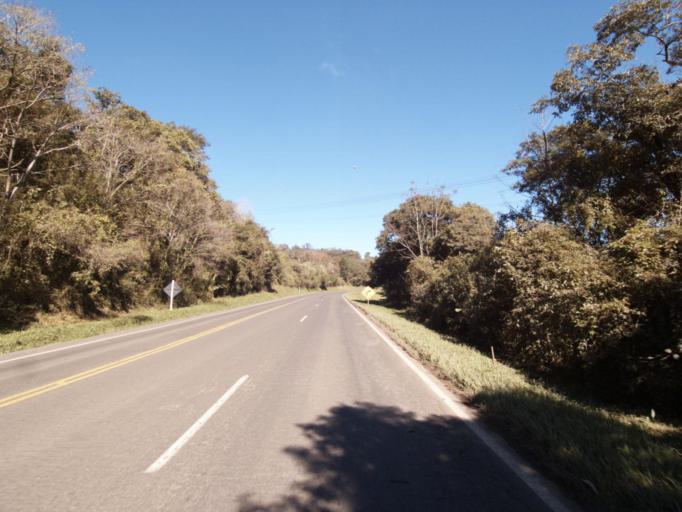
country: BR
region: Santa Catarina
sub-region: Joacaba
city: Joacaba
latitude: -27.1775
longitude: -51.5303
